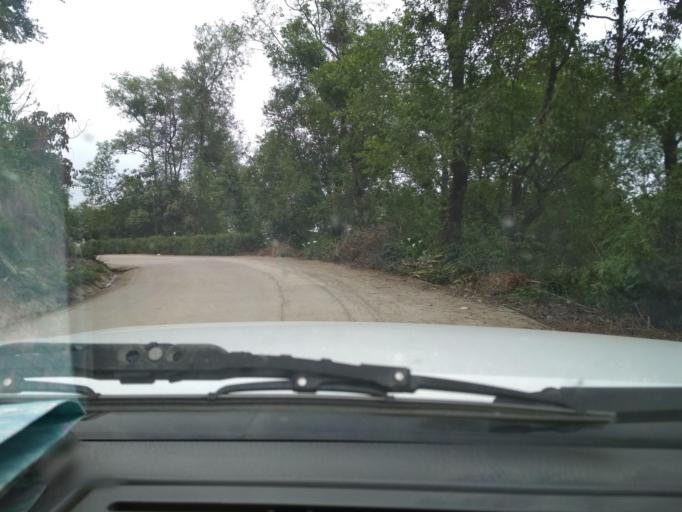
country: MX
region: Veracruz
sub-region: La Perla
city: Chilapa
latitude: 18.9986
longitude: -97.1648
